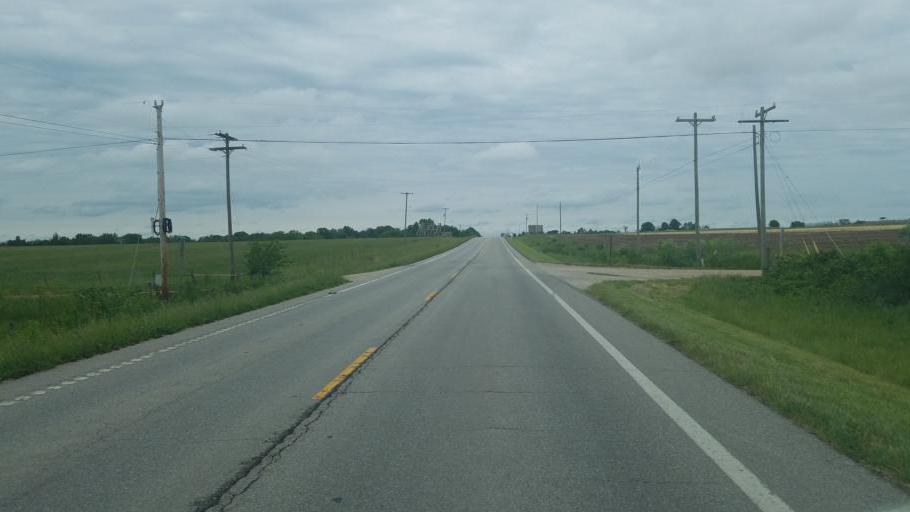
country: US
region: Missouri
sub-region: Morgan County
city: Versailles
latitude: 38.4581
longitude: -92.8092
